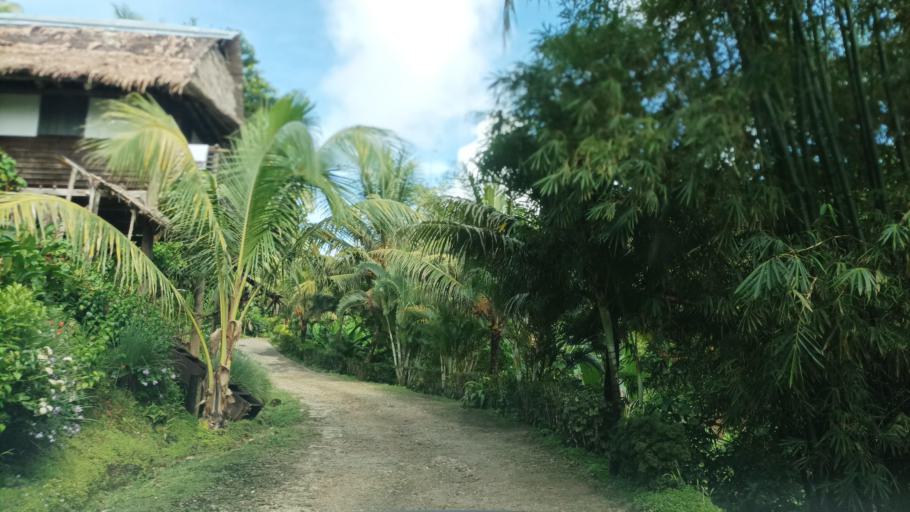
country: FM
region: Pohnpei
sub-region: Kolonia Municipality
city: Kolonia Town
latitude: 6.9606
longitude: 158.2052
